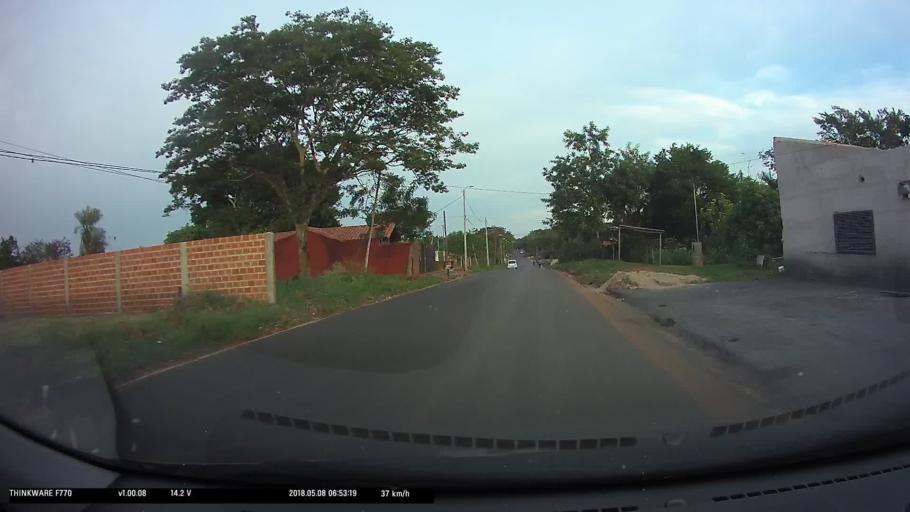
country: PY
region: Central
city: Limpio
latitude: -25.2350
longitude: -57.4698
